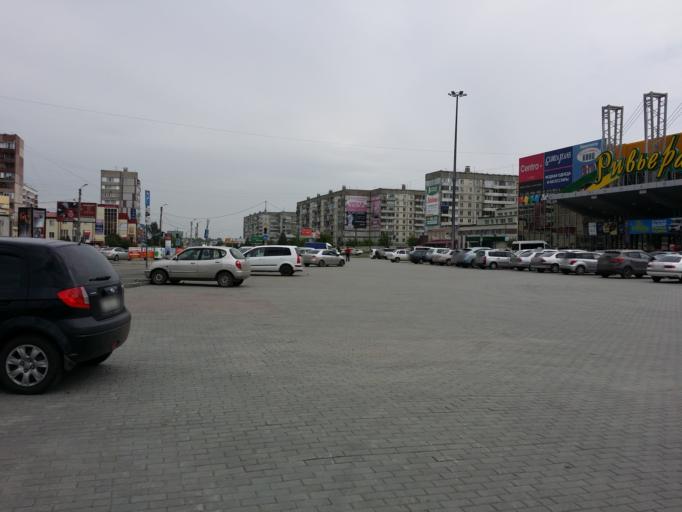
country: RU
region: Altai Krai
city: Biysk
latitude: 52.5126
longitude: 85.1718
